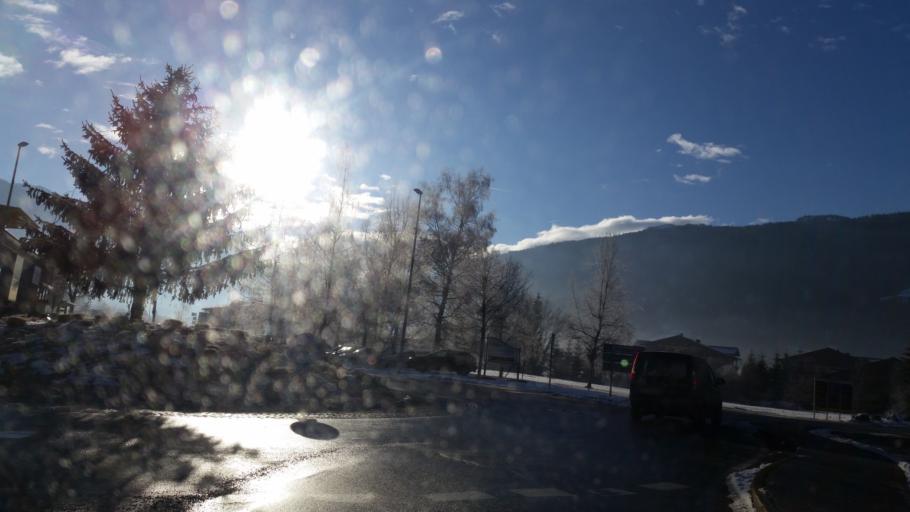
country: AT
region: Salzburg
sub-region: Politischer Bezirk Sankt Johann im Pongau
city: Radstadt
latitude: 47.3781
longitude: 13.4736
